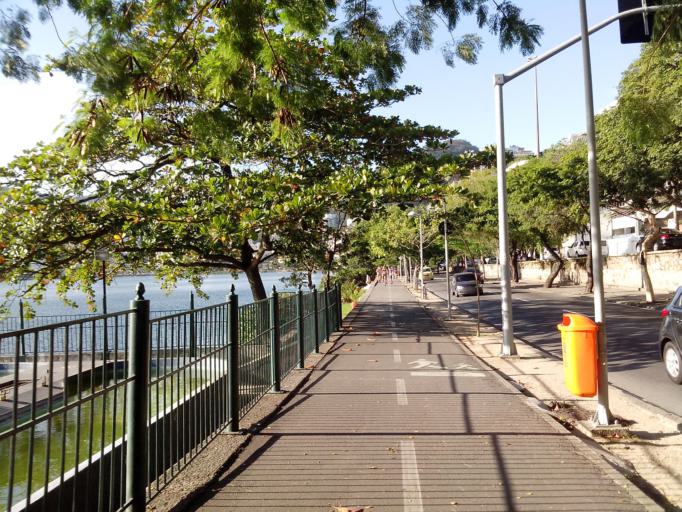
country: BR
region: Rio de Janeiro
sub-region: Rio De Janeiro
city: Rio de Janeiro
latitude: -22.9713
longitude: -43.2075
